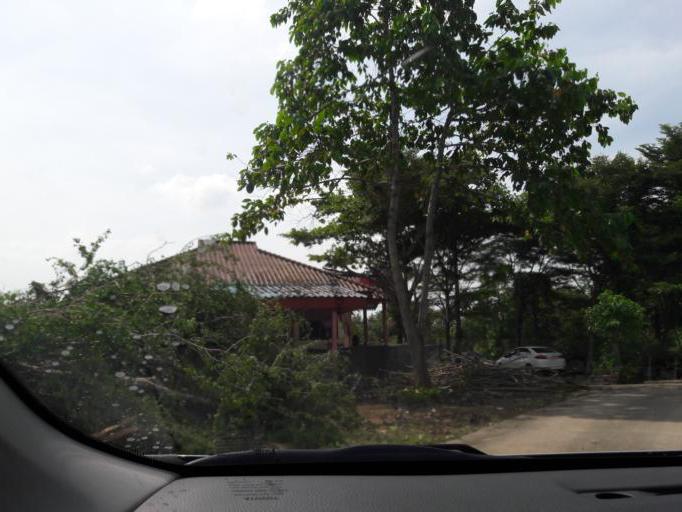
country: TH
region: Ang Thong
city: Ang Thong
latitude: 14.5743
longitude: 100.4416
